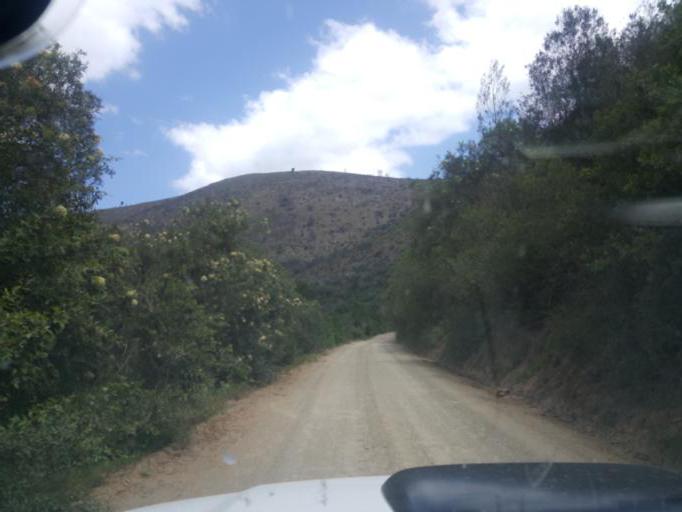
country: ZA
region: Western Cape
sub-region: Eden District Municipality
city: Knysna
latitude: -33.8139
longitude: 23.1750
